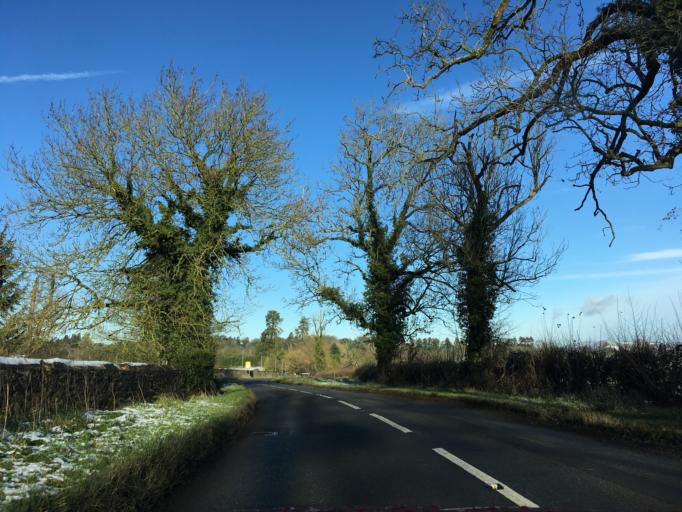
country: GB
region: England
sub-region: South Gloucestershire
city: Falfield
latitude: 51.6253
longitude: -2.4368
